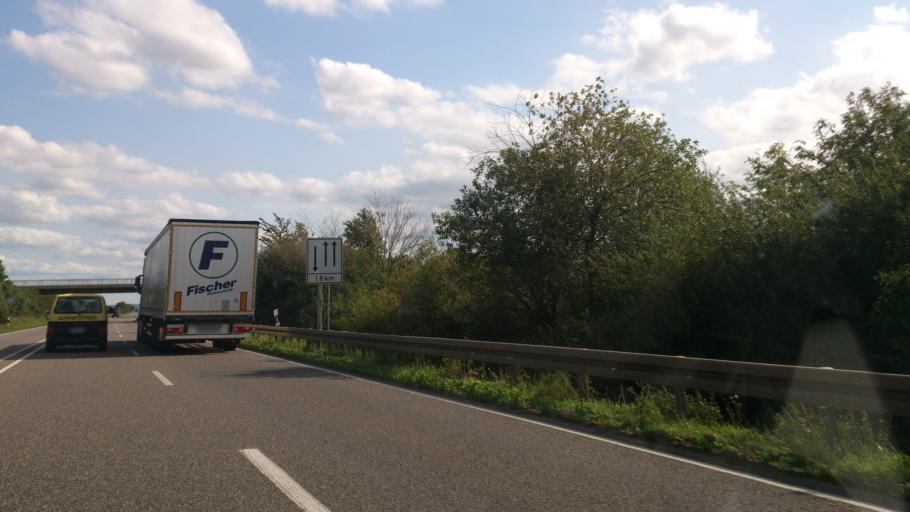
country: DE
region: North Rhine-Westphalia
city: Zulpich
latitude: 50.7089
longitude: 6.6809
